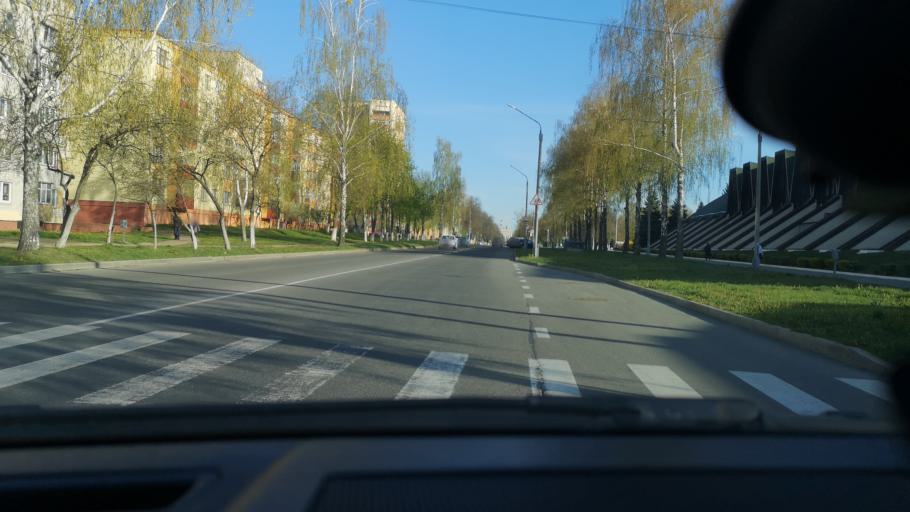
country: BY
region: Gomel
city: Gomel
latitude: 52.4514
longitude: 31.0071
